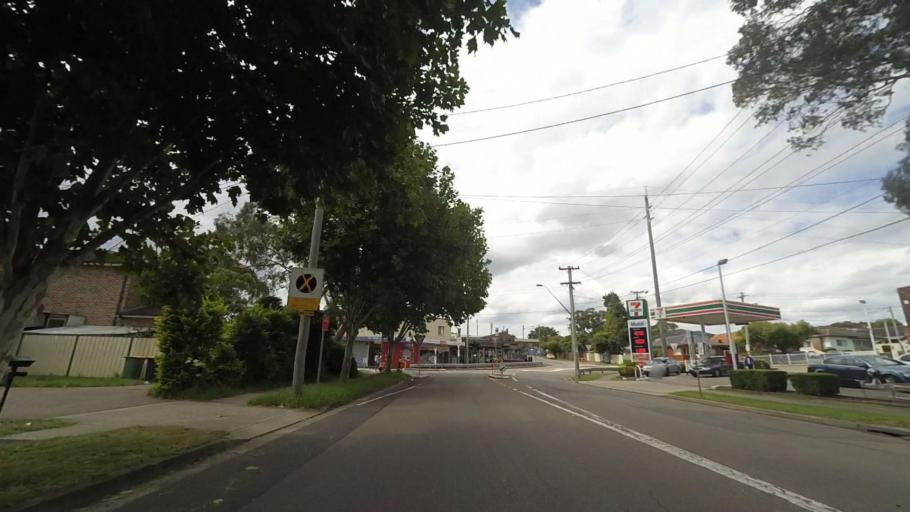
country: AU
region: New South Wales
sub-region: Holroyd
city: Guildford West
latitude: -33.8517
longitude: 150.9719
